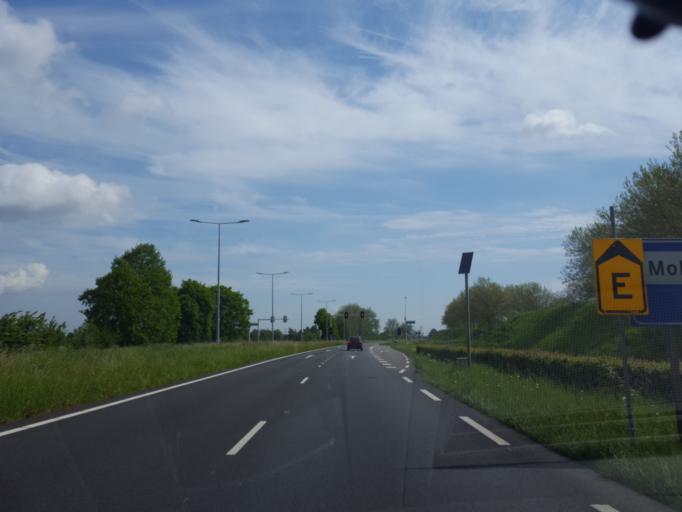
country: NL
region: Limburg
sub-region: Gemeente Weert
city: Weert
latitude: 51.2650
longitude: 5.7049
